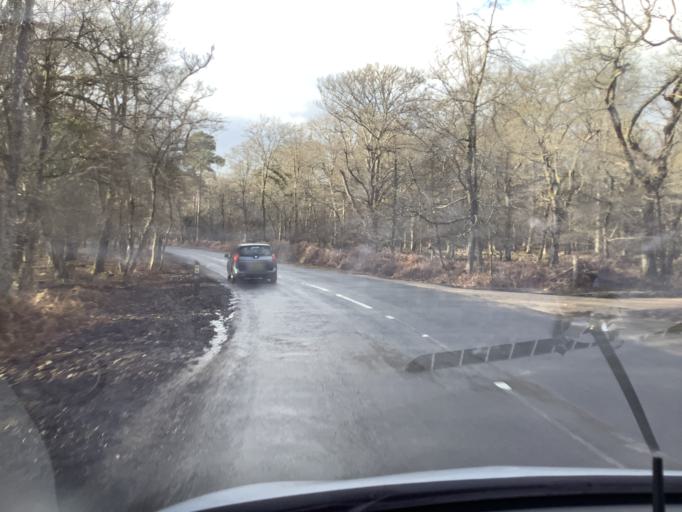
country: GB
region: England
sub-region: Hampshire
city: Brockenhurst
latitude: 50.8190
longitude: -1.5473
